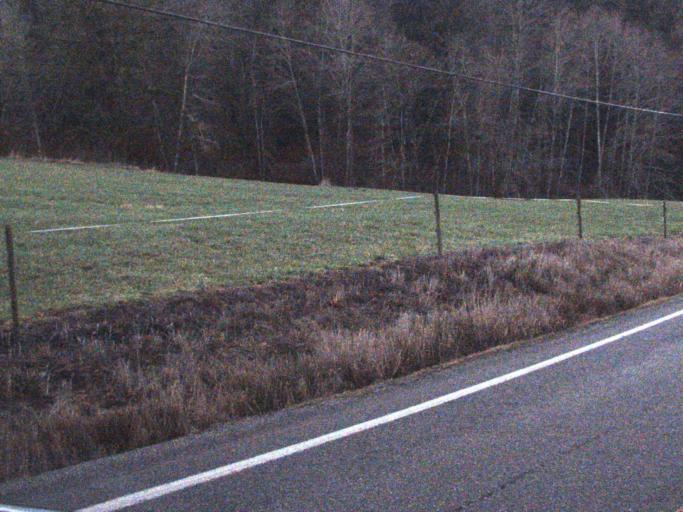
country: US
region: Washington
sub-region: Skagit County
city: Big Lake
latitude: 48.3215
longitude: -122.2467
